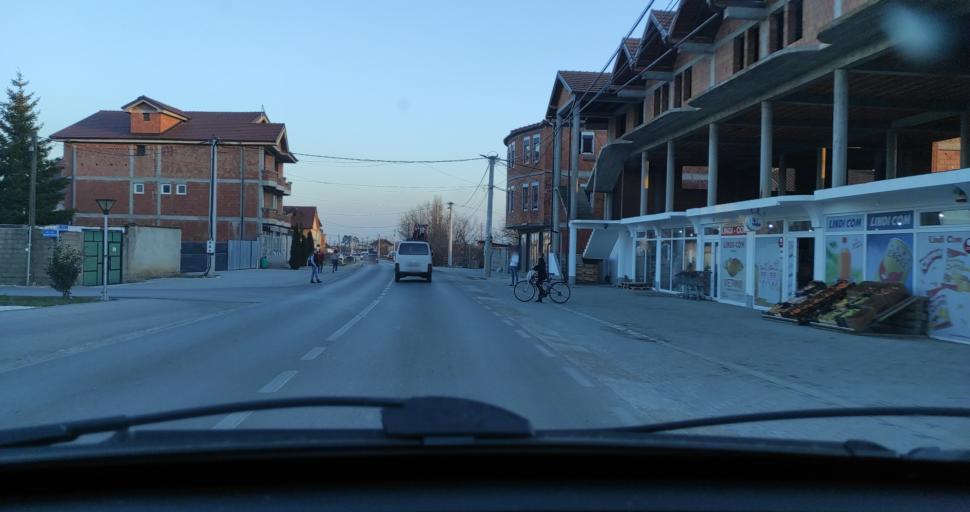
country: XK
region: Gjakova
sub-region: Komuna e Gjakoves
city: Gjakove
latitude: 42.4303
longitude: 20.3835
